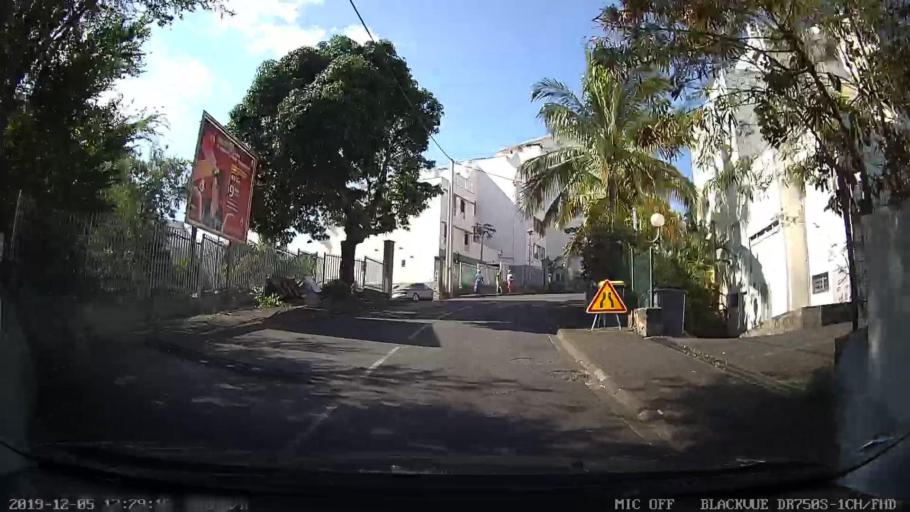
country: RE
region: Reunion
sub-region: Reunion
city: Saint-Denis
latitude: -20.8957
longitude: 55.4818
